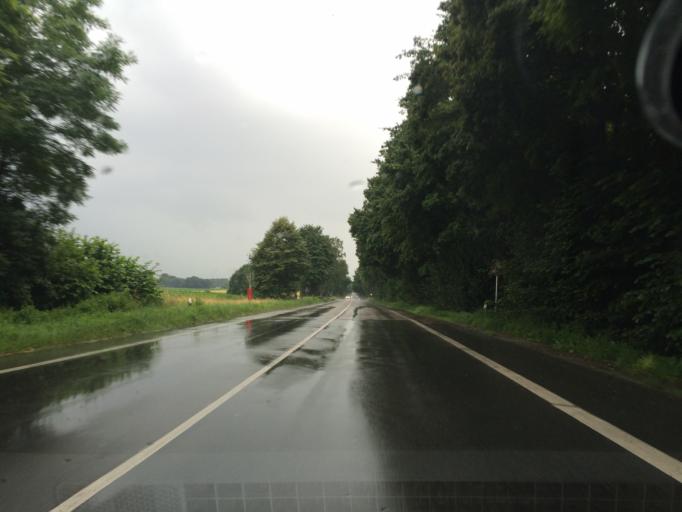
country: DE
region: North Rhine-Westphalia
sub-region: Regierungsbezirk Munster
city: Haltern
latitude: 51.7775
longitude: 7.2060
